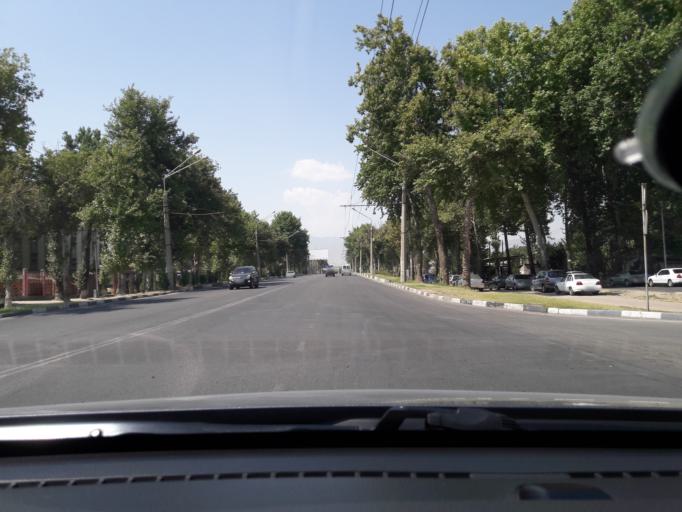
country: TJ
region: Dushanbe
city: Dushanbe
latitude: 38.5732
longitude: 68.7548
